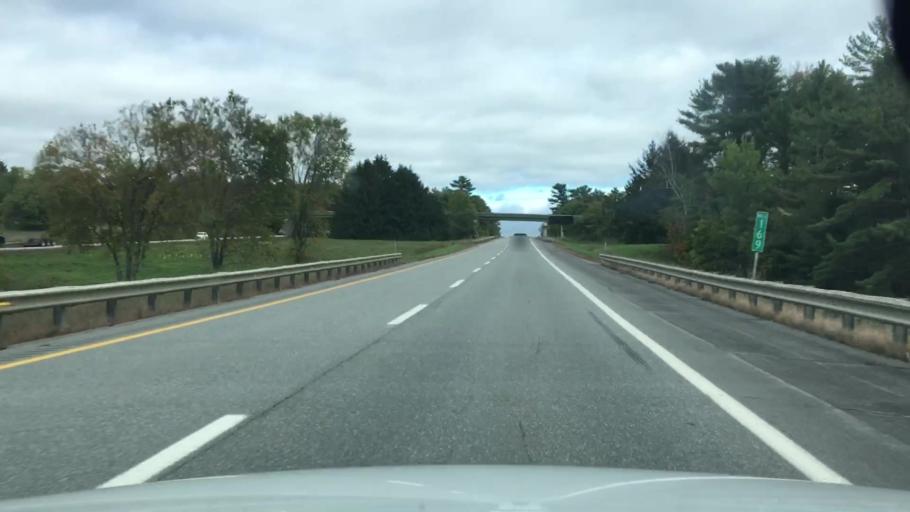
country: US
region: Maine
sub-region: Penobscot County
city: Carmel
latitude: 44.7786
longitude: -69.0650
